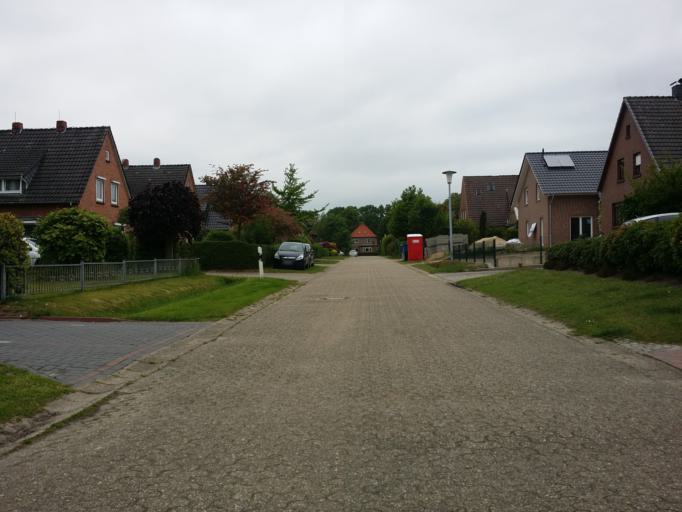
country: DE
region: Lower Saxony
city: Oldenburg
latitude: 53.1858
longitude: 8.2466
